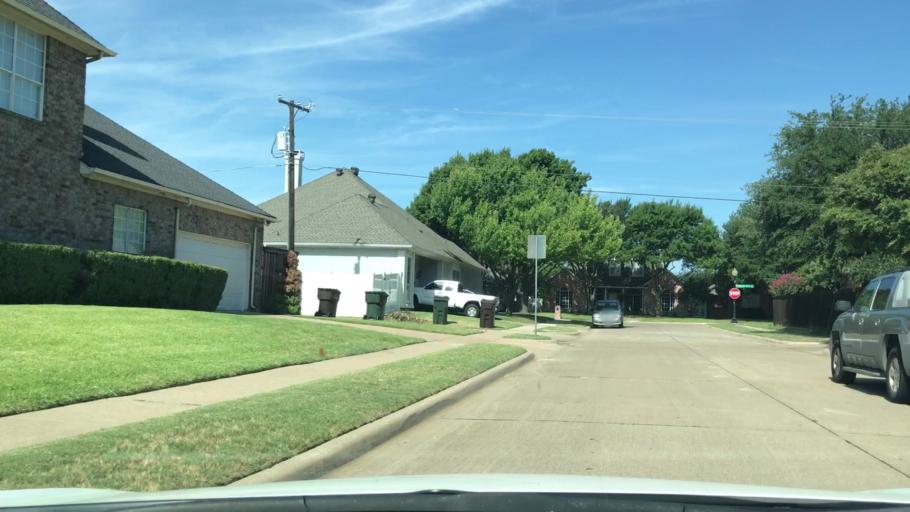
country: US
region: Texas
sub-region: Collin County
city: Plano
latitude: 33.0543
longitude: -96.7642
